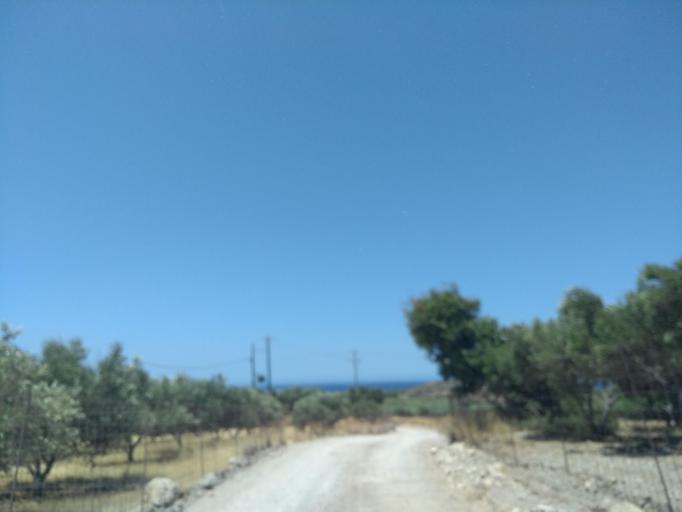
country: GR
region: Crete
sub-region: Nomos Chanias
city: Vryses
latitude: 35.3035
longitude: 23.5398
